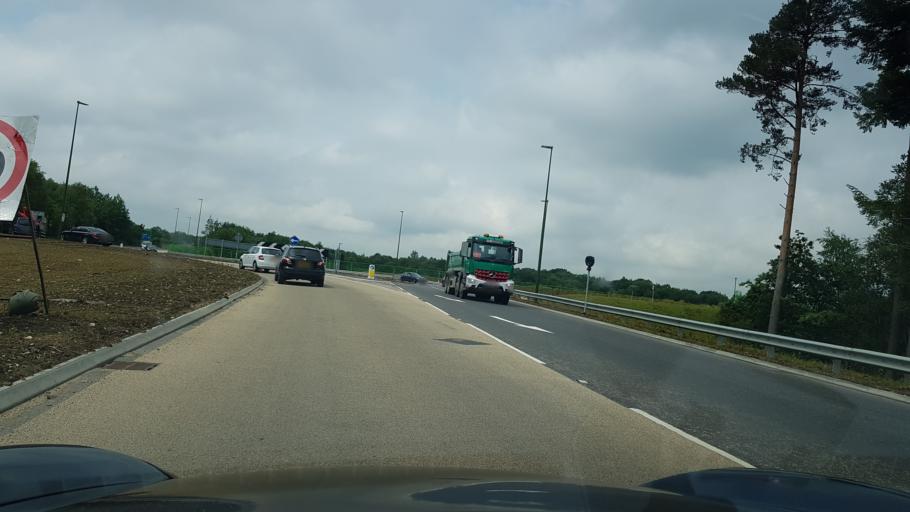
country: GB
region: England
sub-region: West Sussex
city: Copthorne
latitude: 51.1330
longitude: -0.1344
